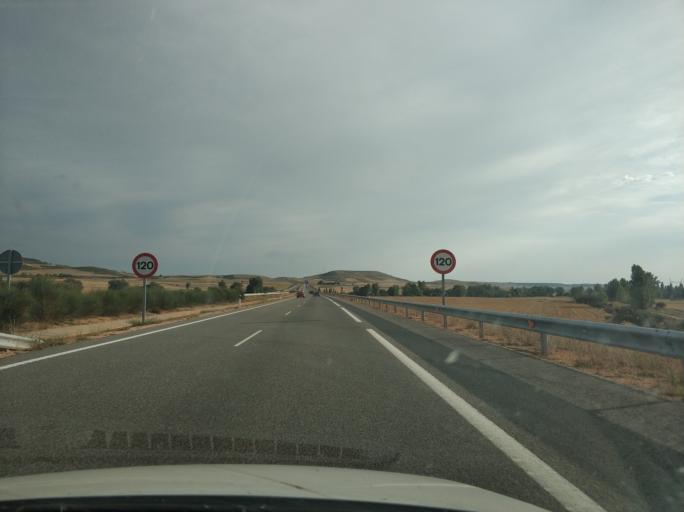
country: ES
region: Castille and Leon
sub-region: Provincia de Burgos
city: Sotragero
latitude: 42.4151
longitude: -3.6970
